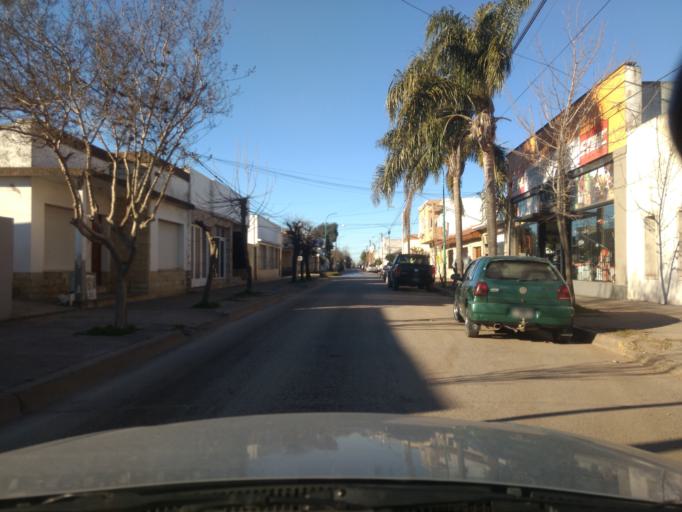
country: AR
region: Buenos Aires
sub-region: Partido de Navarro
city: Navarro
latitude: -35.0021
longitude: -59.2808
